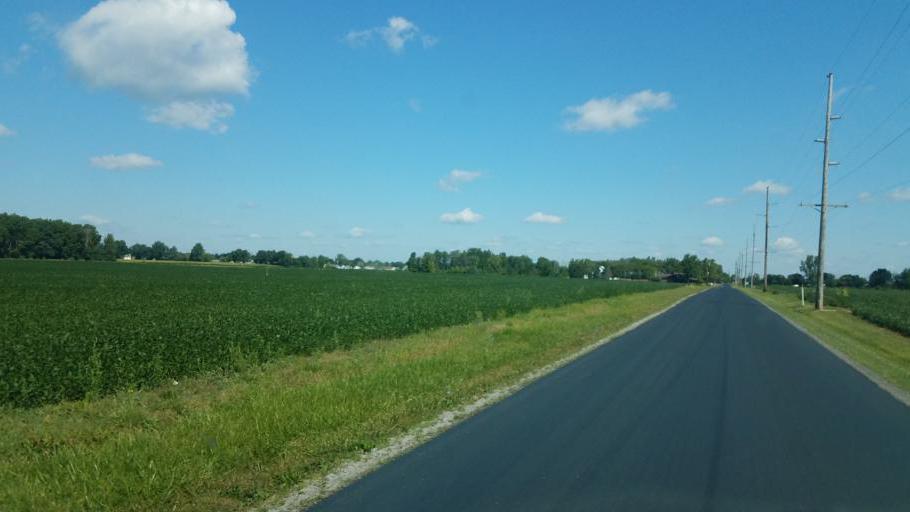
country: US
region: Ohio
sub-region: Wyandot County
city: Carey
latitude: 40.9361
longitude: -83.3674
